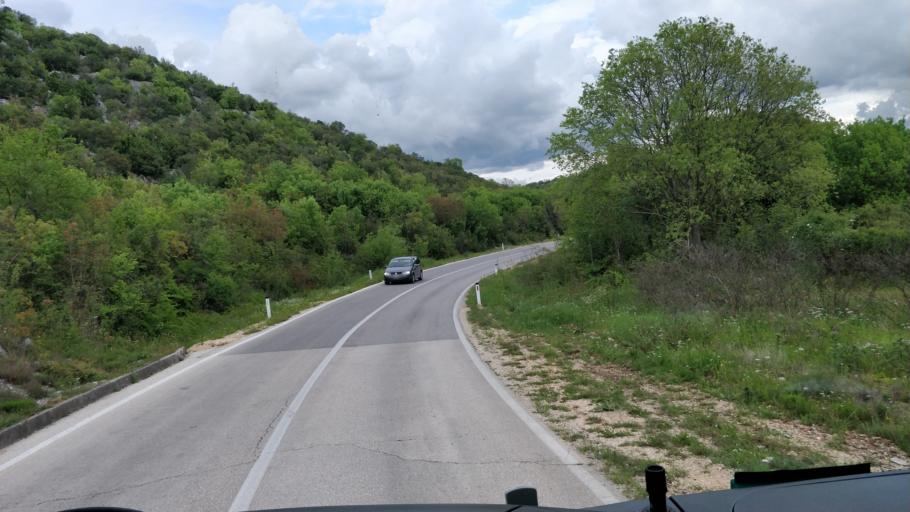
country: BA
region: Federation of Bosnia and Herzegovina
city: Vitina
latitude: 43.1738
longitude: 17.4850
